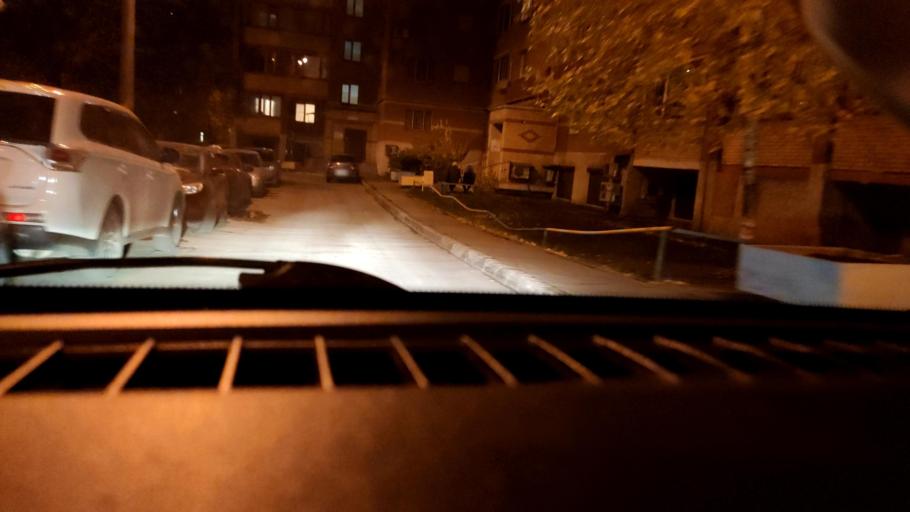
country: RU
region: Samara
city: Samara
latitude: 53.2041
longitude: 50.2258
